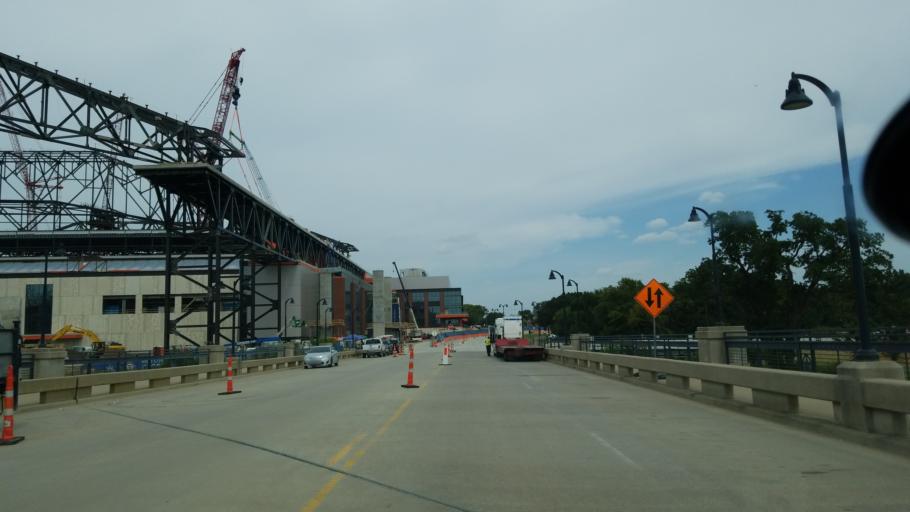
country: US
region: Texas
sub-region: Tarrant County
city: Arlington
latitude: 32.7462
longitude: -97.0871
